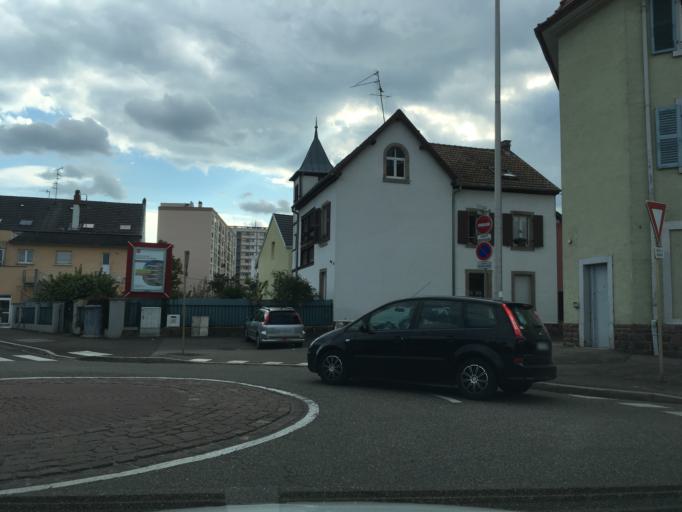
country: FR
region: Alsace
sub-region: Departement du Haut-Rhin
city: Colmar
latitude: 48.0861
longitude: 7.3571
